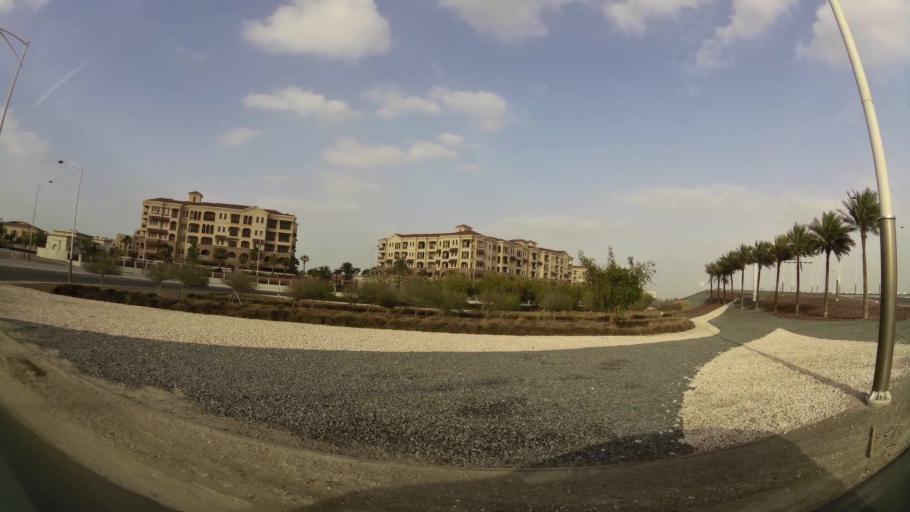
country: AE
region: Abu Dhabi
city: Abu Dhabi
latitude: 24.5482
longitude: 54.4515
